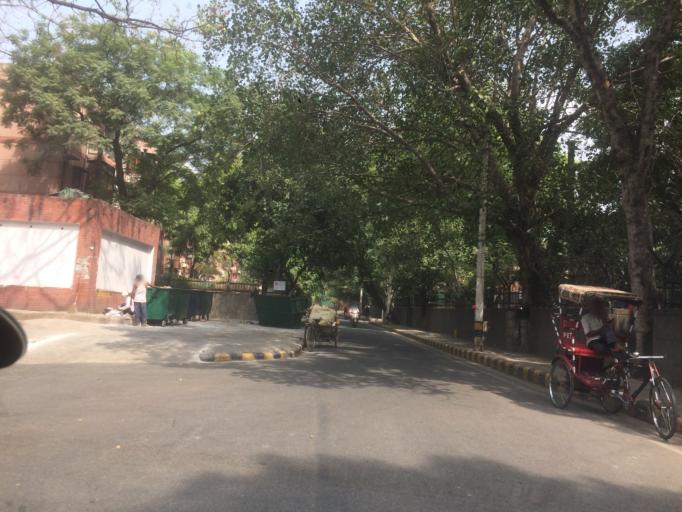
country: IN
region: NCT
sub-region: New Delhi
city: New Delhi
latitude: 28.6383
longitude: 77.2050
